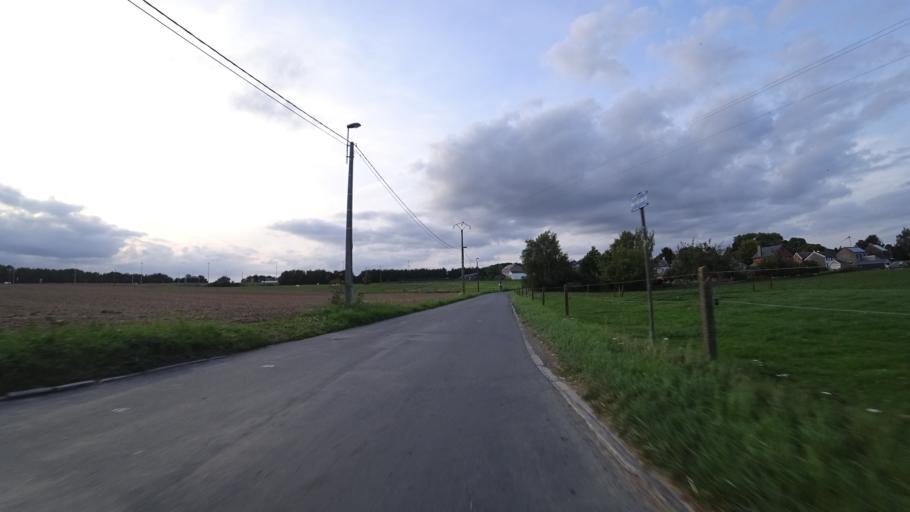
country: BE
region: Wallonia
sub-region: Province de Namur
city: Namur
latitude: 50.5142
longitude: 4.8701
